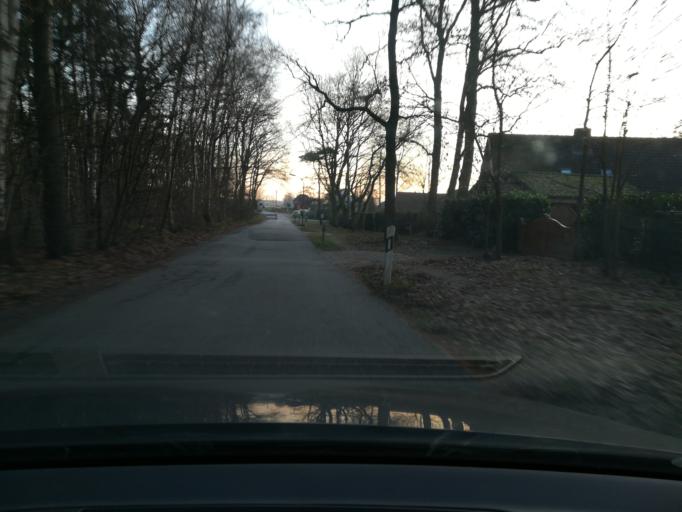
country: DE
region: Schleswig-Holstein
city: Escheburg
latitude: 53.4449
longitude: 10.3104
